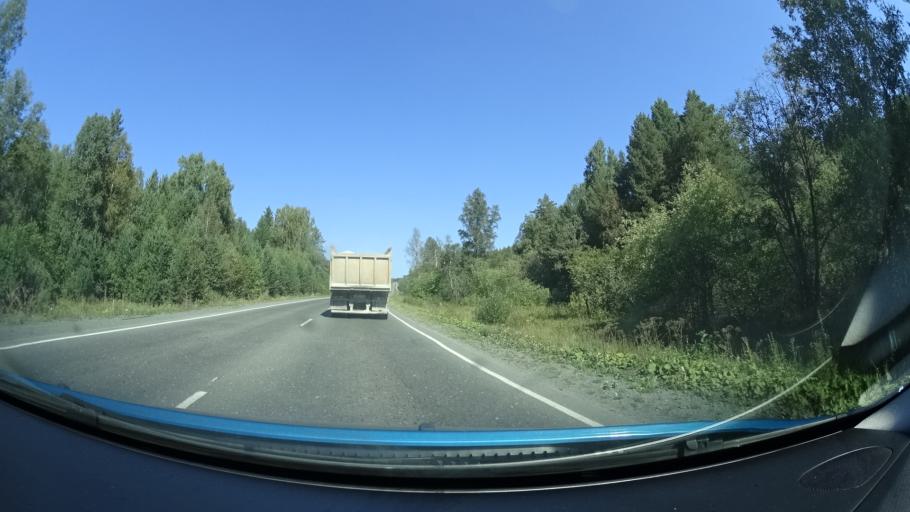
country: RU
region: Bashkortostan
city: Abzakovo
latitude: 53.8681
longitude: 58.5391
